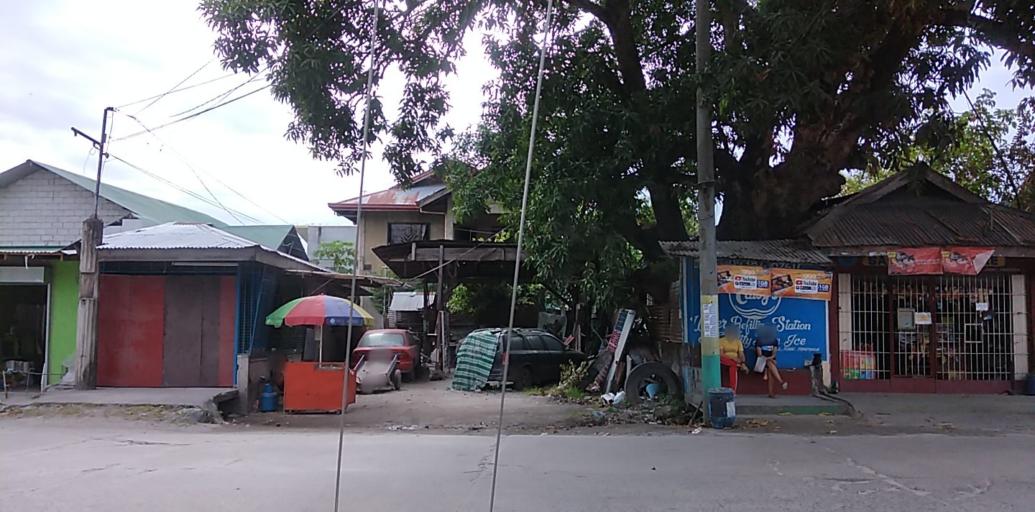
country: PH
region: Central Luzon
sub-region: Province of Pampanga
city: Pulung Santol
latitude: 15.0505
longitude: 120.5570
